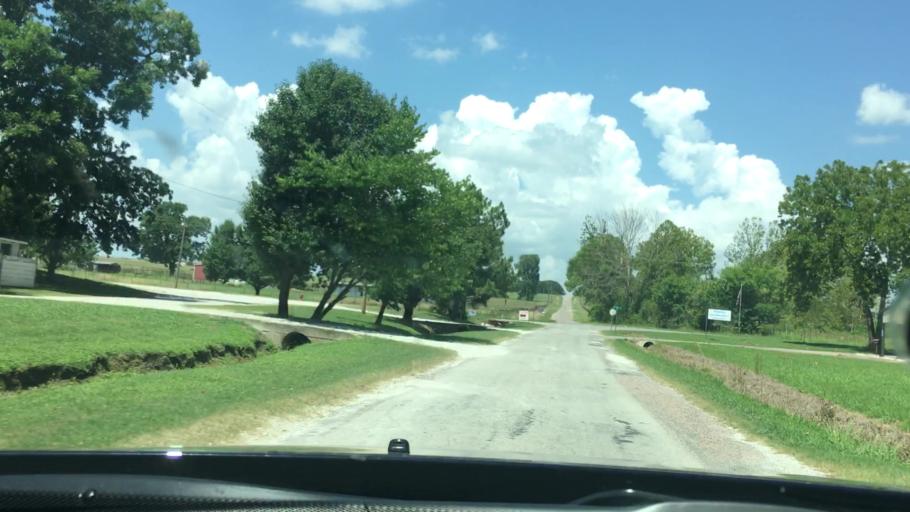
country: US
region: Oklahoma
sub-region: Pontotoc County
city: Ada
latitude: 34.6945
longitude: -96.5815
